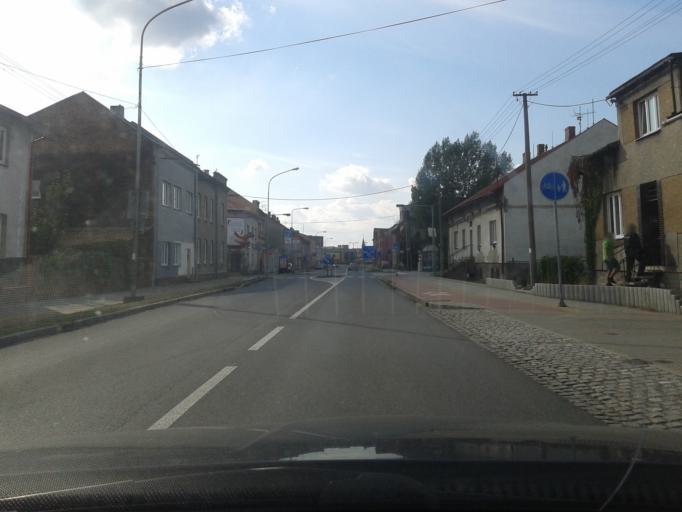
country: CZ
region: Moravskoslezsky
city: Bohumin
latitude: 49.9043
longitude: 18.3731
